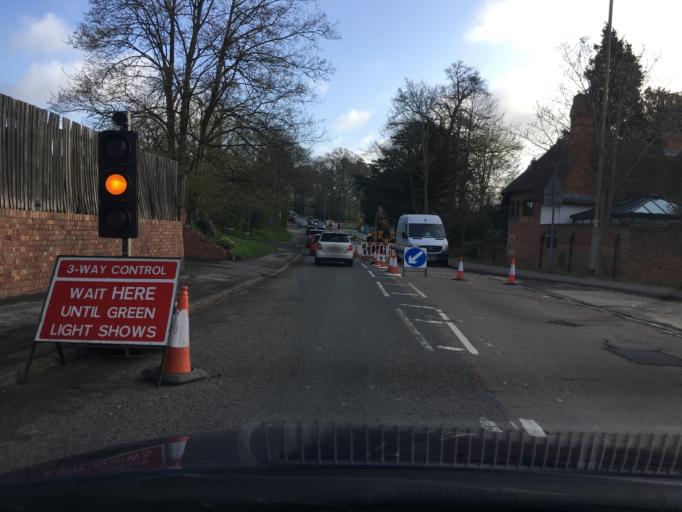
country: GB
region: England
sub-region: Bracknell Forest
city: Sandhurst
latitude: 51.3500
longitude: -0.8012
